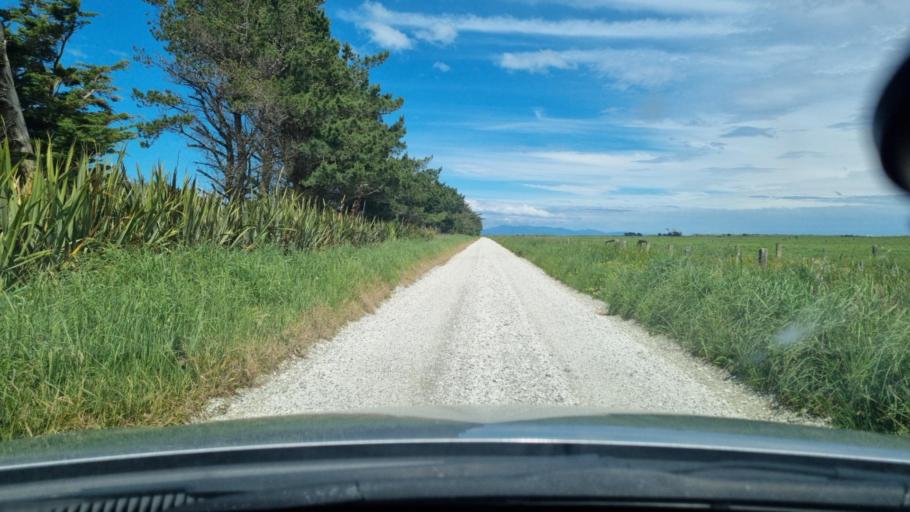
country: NZ
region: Southland
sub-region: Invercargill City
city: Invercargill
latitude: -46.3824
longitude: 168.2679
